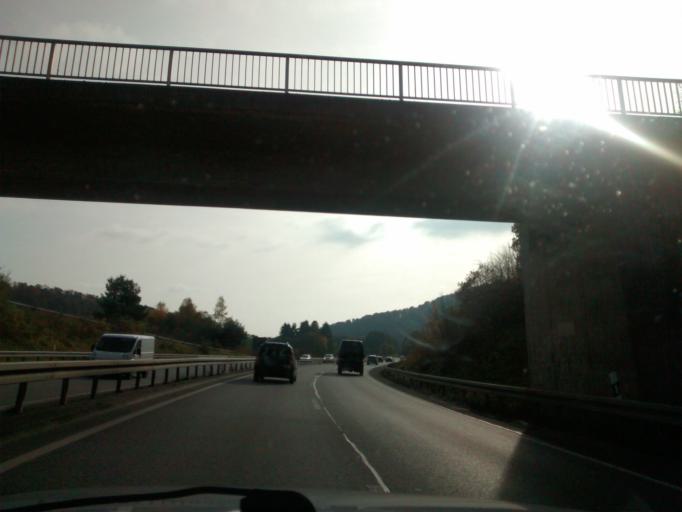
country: DE
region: Hesse
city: Dillenburg
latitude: 50.7141
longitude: 8.3052
